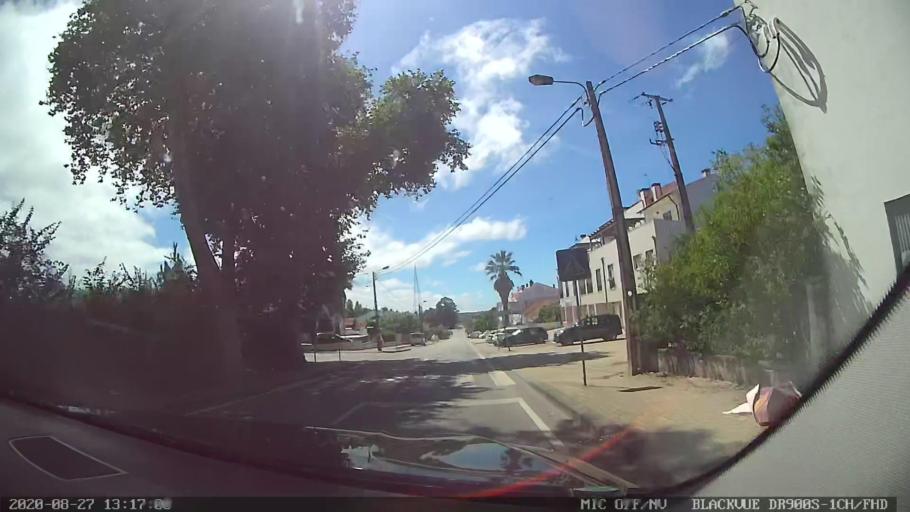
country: PT
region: Aveiro
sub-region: Ilhavo
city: Ilhavo
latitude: 40.5846
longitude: -8.6796
